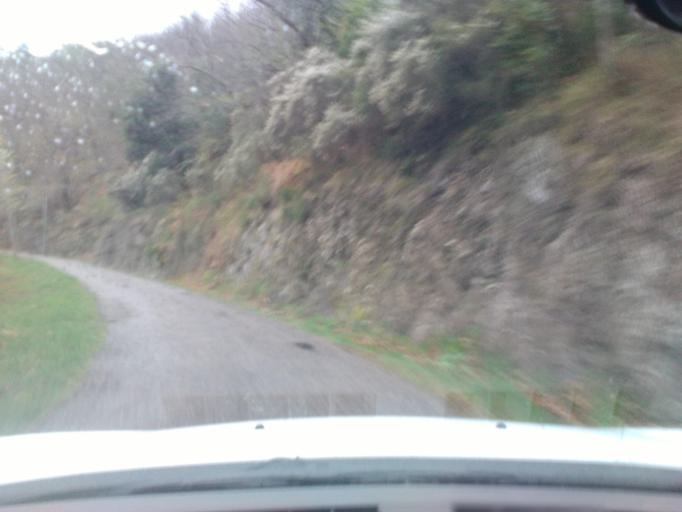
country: FR
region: Languedoc-Roussillon
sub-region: Departement du Gard
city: Valleraugue
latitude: 44.1089
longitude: 3.6691
